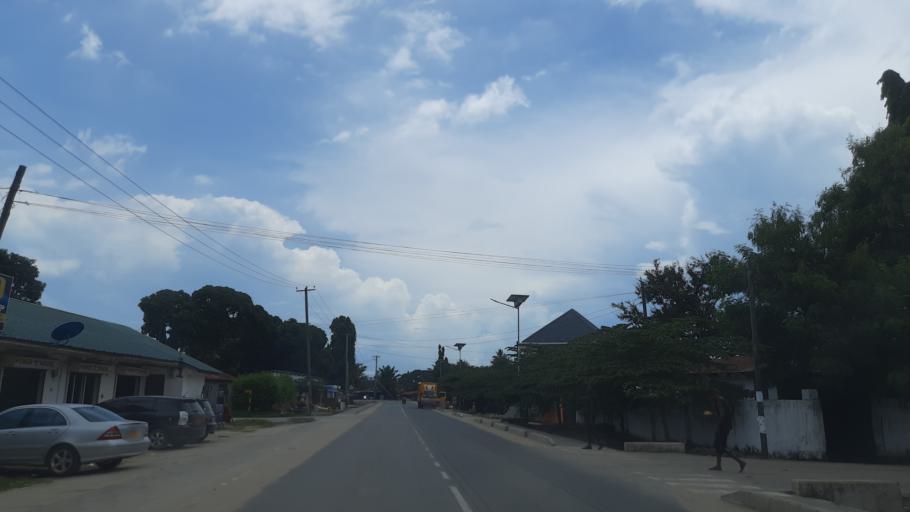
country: TZ
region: Dar es Salaam
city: Magomeni
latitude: -6.7735
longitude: 39.2298
